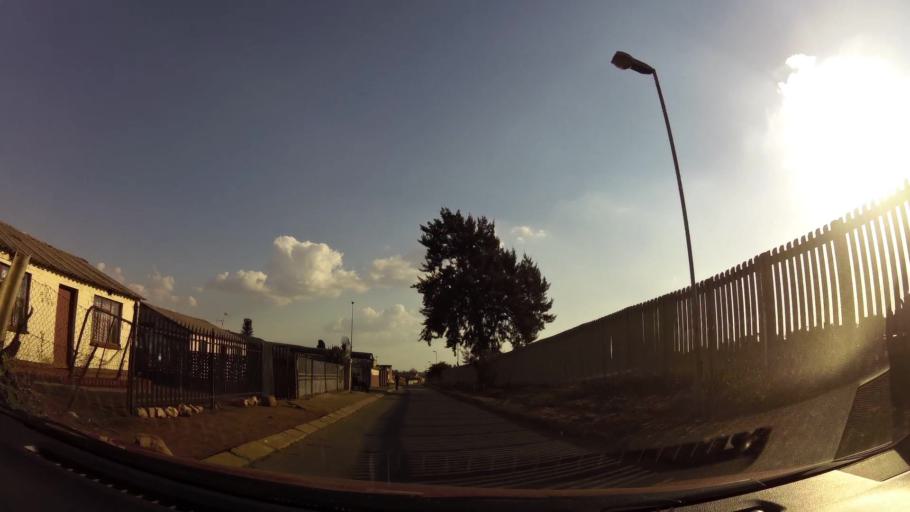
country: ZA
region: Gauteng
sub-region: City of Johannesburg Metropolitan Municipality
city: Soweto
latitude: -26.2373
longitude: 27.8544
